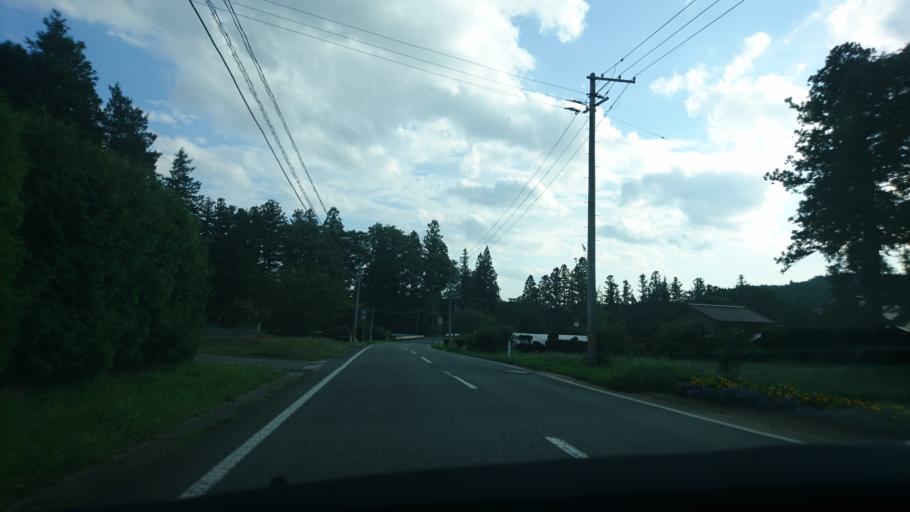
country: JP
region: Iwate
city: Mizusawa
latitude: 39.0270
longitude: 141.2939
